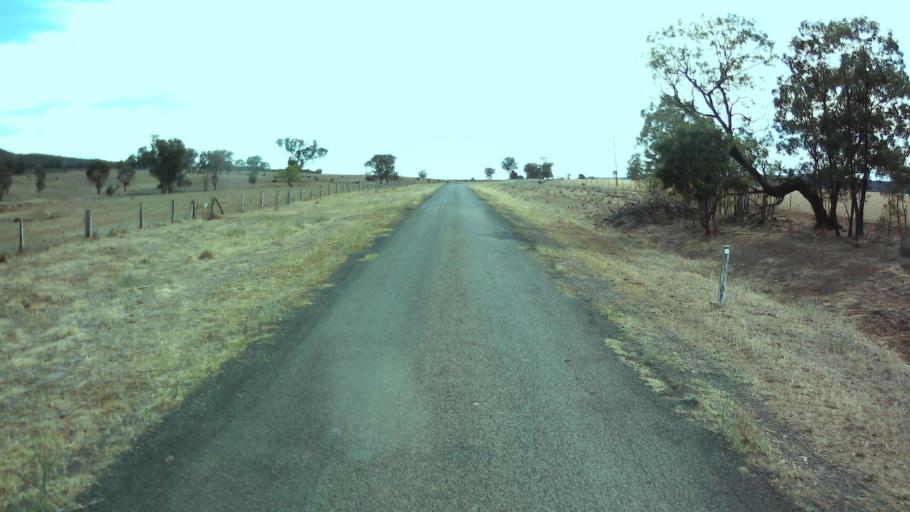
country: AU
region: New South Wales
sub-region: Weddin
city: Grenfell
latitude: -33.8366
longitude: 148.2684
